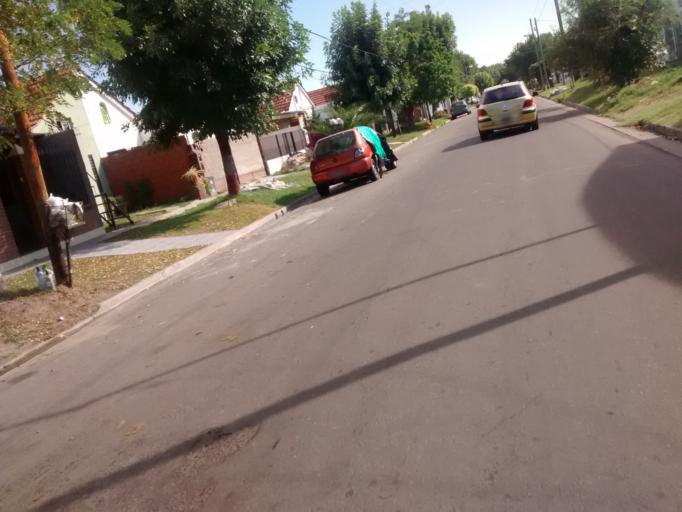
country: AR
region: Buenos Aires
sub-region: Partido de La Plata
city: La Plata
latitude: -34.9518
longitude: -57.9465
